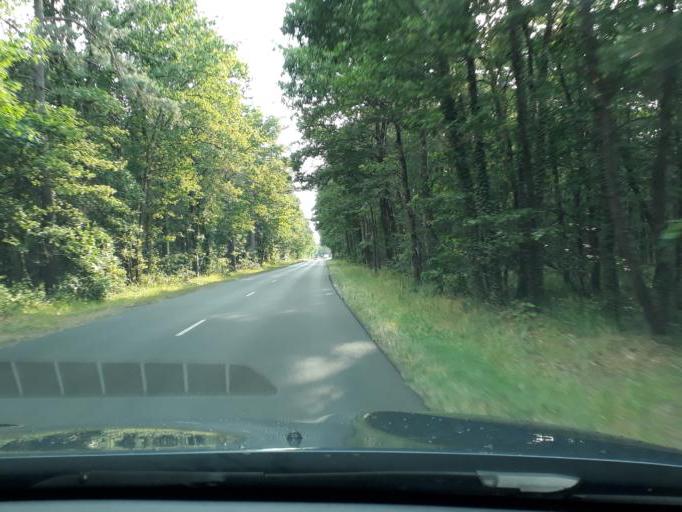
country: FR
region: Centre
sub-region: Departement du Loiret
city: Saint-Cyr-en-Val
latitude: 47.8207
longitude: 1.9620
